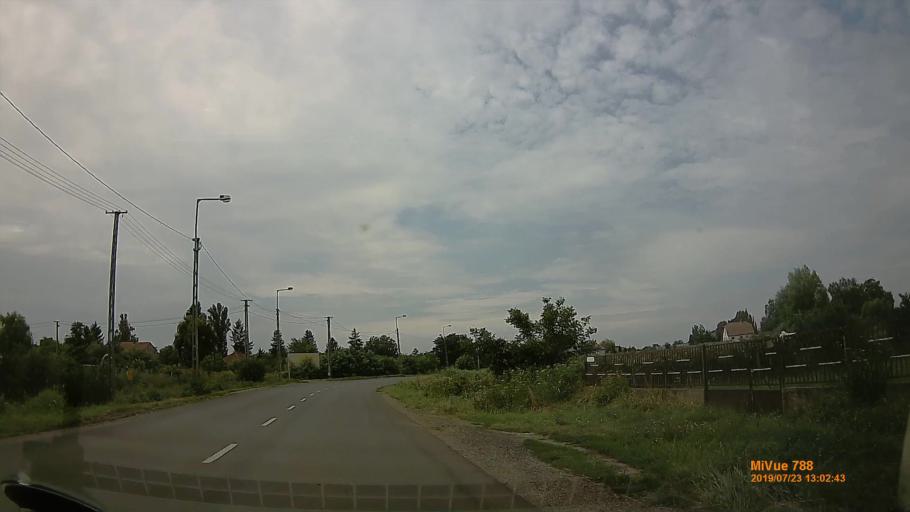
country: HU
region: Szabolcs-Szatmar-Bereg
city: Tiszavasvari
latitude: 47.9565
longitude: 21.3814
